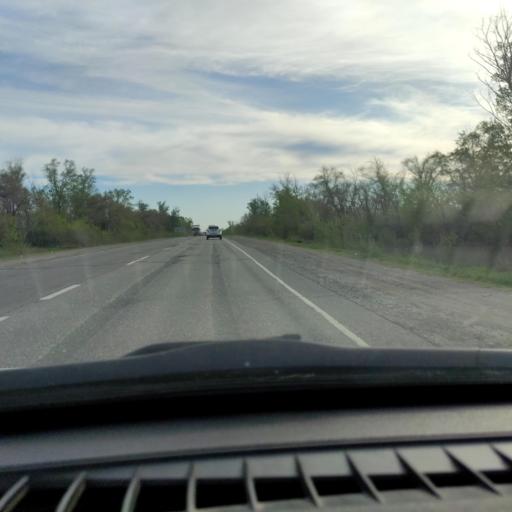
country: RU
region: Samara
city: Bereza
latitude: 53.4707
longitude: 50.1939
